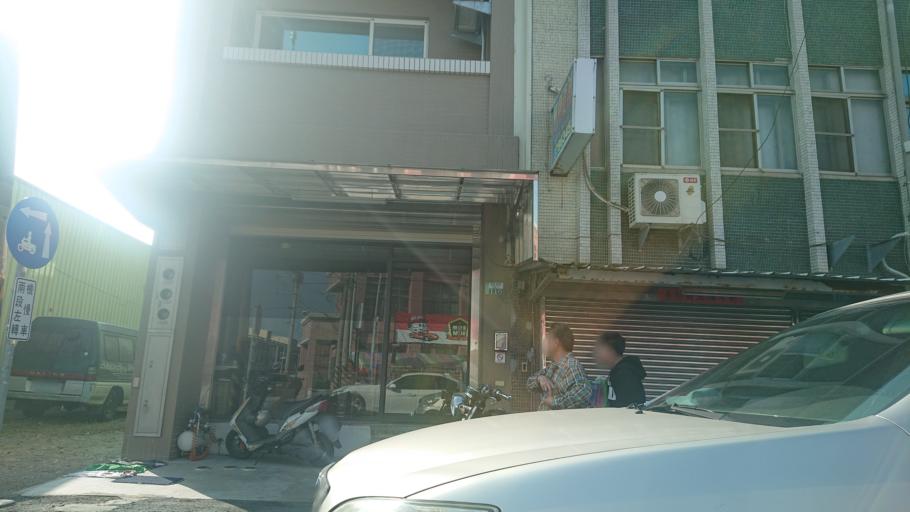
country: TW
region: Taiwan
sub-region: Chiayi
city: Taibao
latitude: 23.4589
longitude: 120.2409
